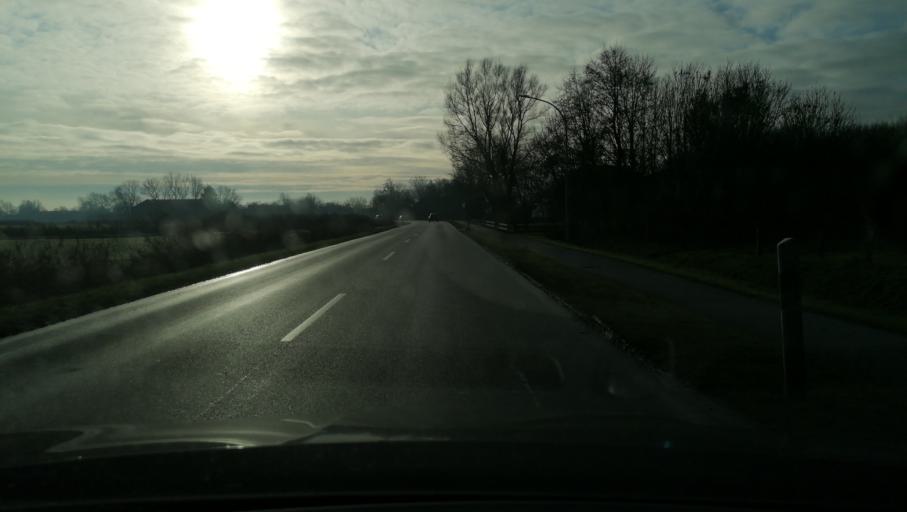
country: DE
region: Schleswig-Holstein
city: Epenwohrden
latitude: 54.1200
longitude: 9.0159
